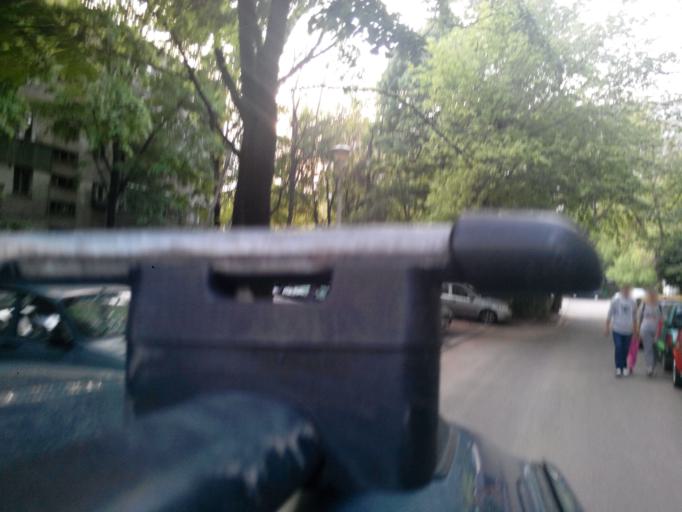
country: RO
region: Ilfov
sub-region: Comuna Chiajna
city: Rosu
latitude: 44.4360
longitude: 26.0193
